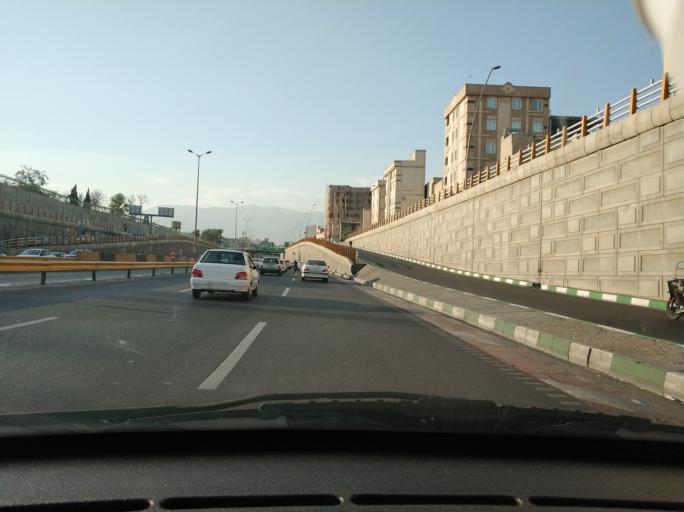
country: IR
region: Tehran
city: Tehran
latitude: 35.6911
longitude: 51.4573
